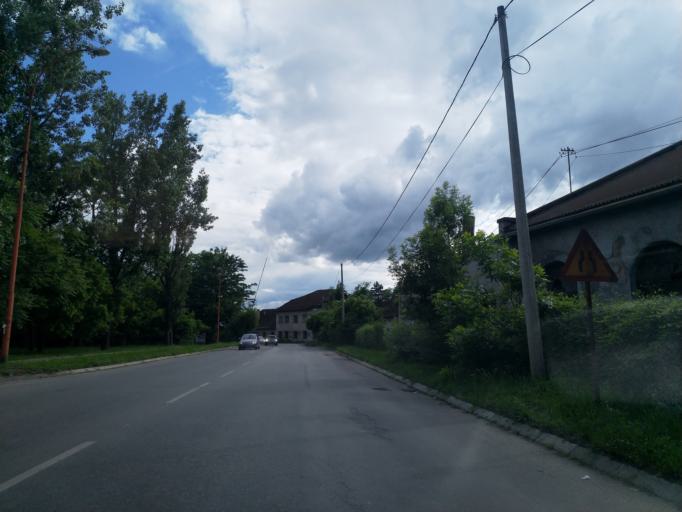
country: RS
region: Central Serbia
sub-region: Pomoravski Okrug
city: Cuprija
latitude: 43.9165
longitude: 21.3762
